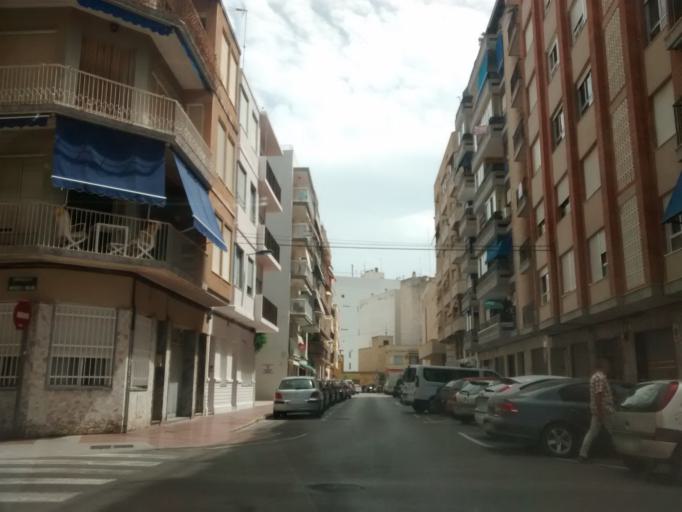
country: ES
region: Valencia
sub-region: Provincia de Alicante
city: Santa Pola
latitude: 38.1916
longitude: -0.5584
